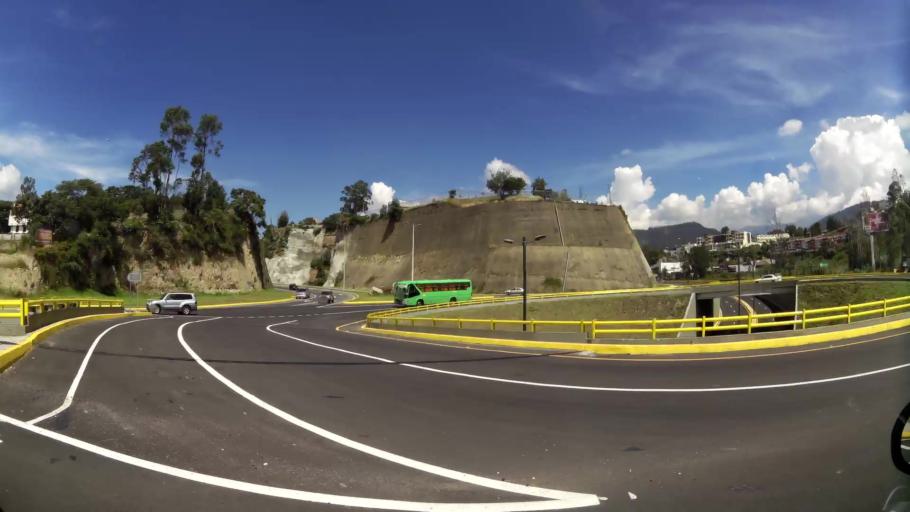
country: EC
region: Pichincha
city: Quito
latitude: -0.2052
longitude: -78.4299
